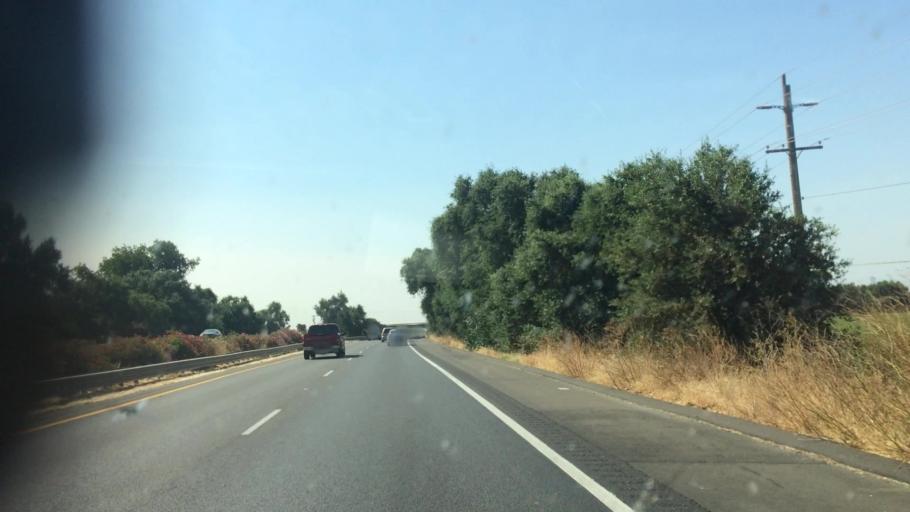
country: US
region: California
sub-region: Sacramento County
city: Elk Grove
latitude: 38.3462
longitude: -121.3372
